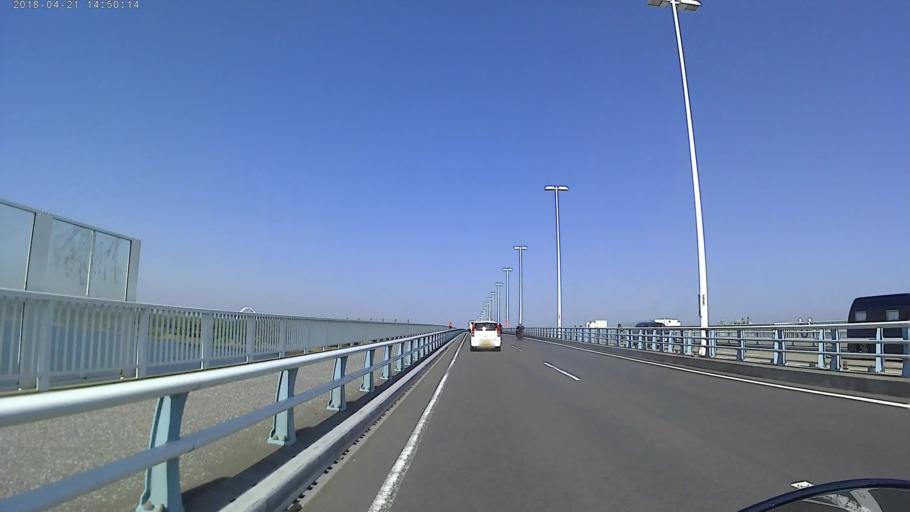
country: JP
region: Kanagawa
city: Hiratsuka
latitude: 35.3180
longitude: 139.3669
